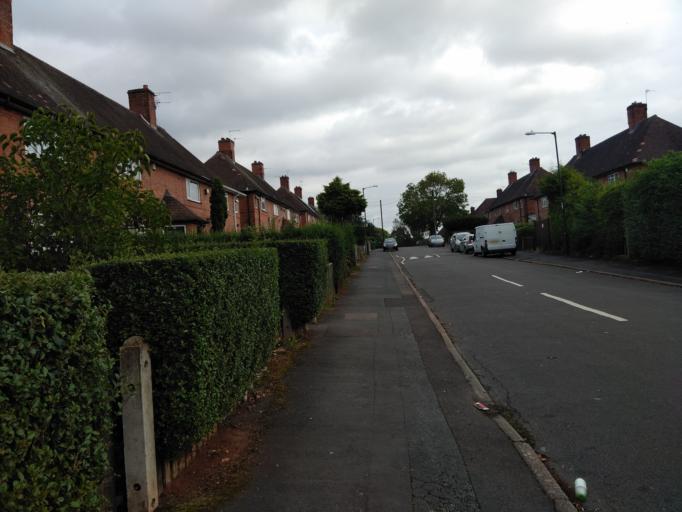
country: GB
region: England
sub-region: Nottinghamshire
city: Kimberley
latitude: 52.9693
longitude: -1.2183
